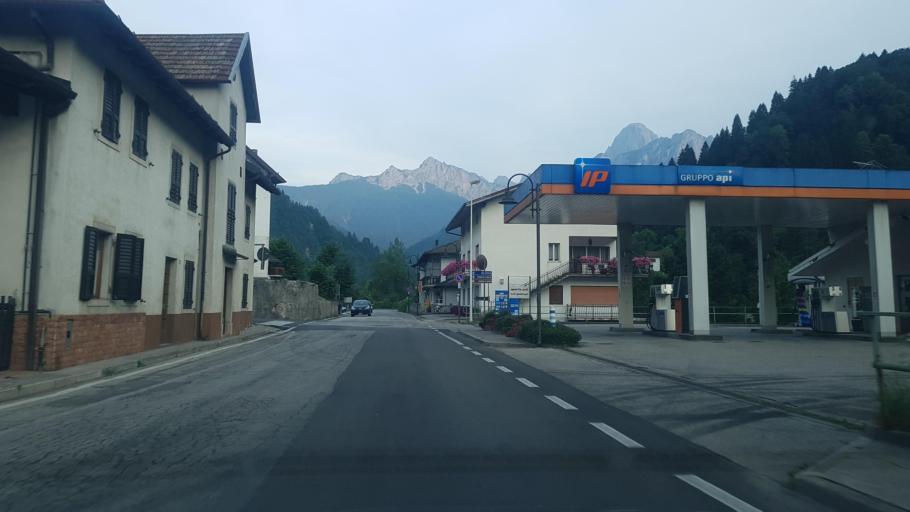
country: IT
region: Friuli Venezia Giulia
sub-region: Provincia di Udine
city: Paularo
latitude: 46.5276
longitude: 13.1192
